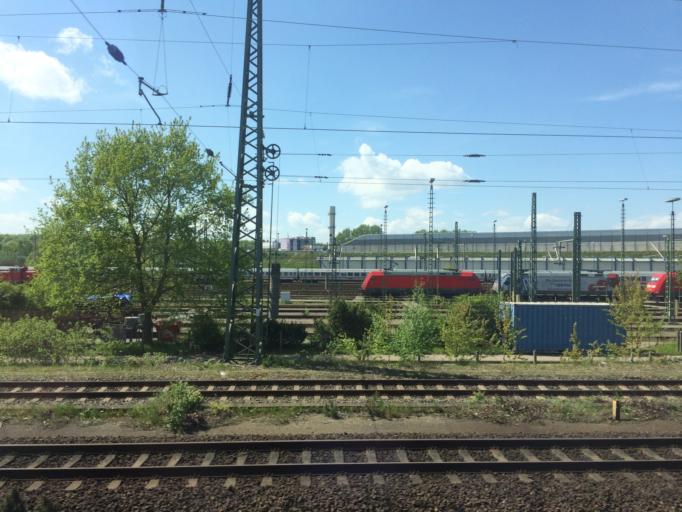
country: DE
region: Hamburg
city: Stellingen
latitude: 53.5876
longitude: 9.9197
